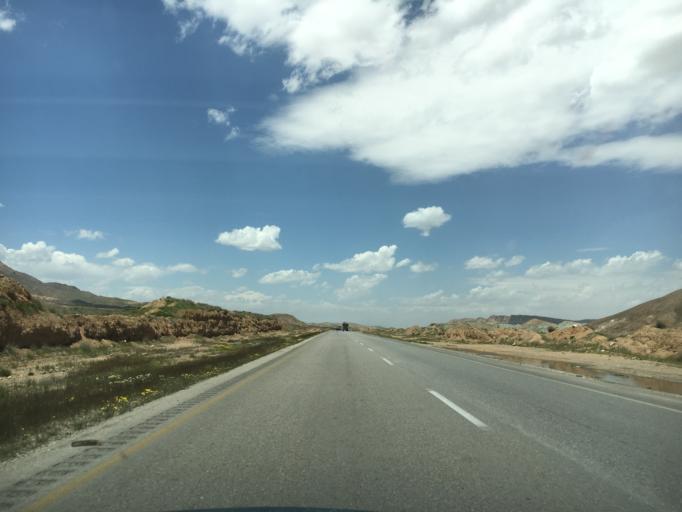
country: IR
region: Markazi
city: Delijan
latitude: 33.8191
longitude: 50.8269
